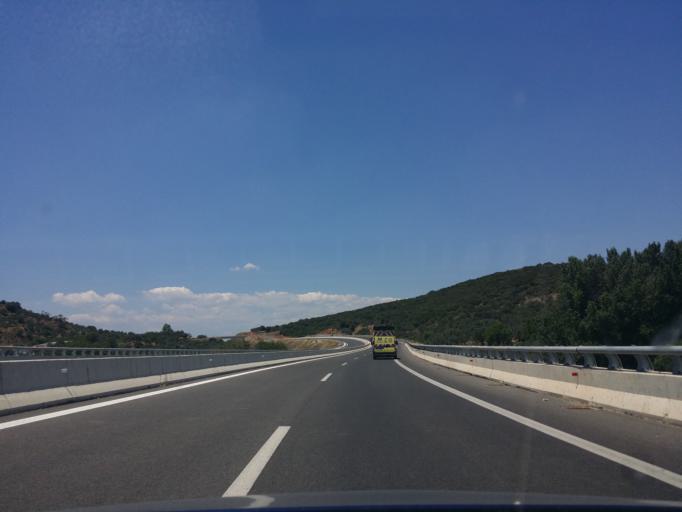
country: GR
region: Peloponnese
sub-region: Nomos Lakonias
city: Magoula
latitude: 37.1213
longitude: 22.4117
